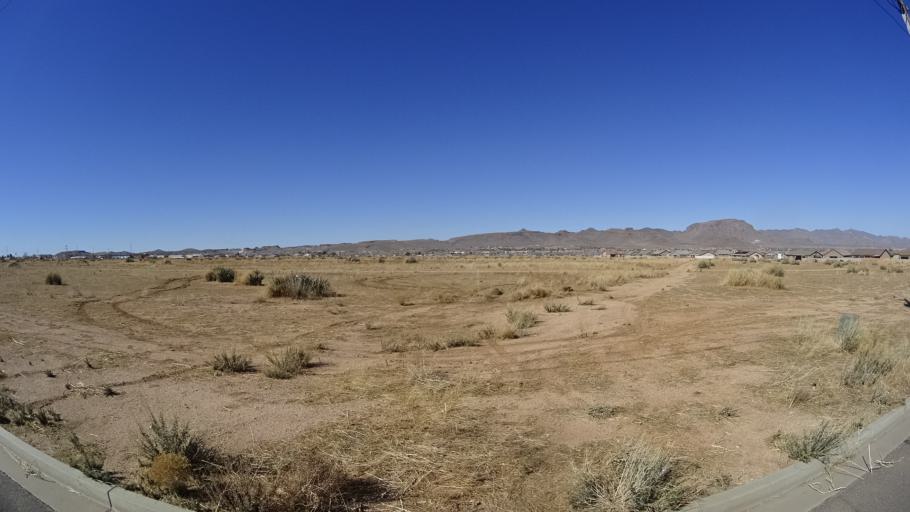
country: US
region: Arizona
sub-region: Mohave County
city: New Kingman-Butler
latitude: 35.2298
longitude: -114.0054
